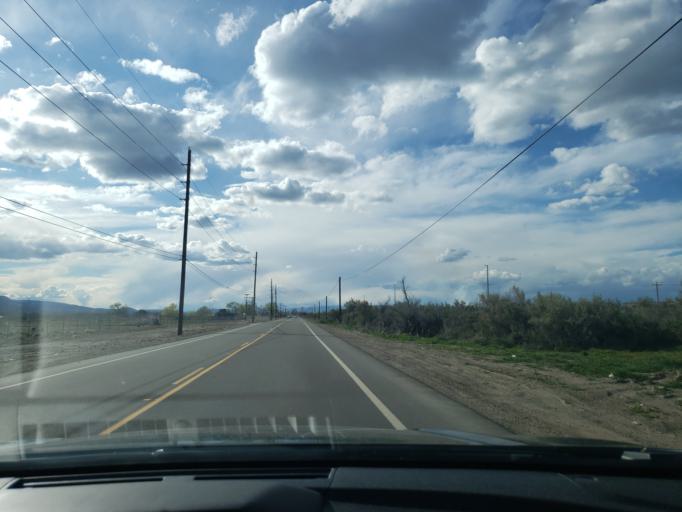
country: US
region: Colorado
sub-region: Mesa County
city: Redlands
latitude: 39.1143
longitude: -108.6546
